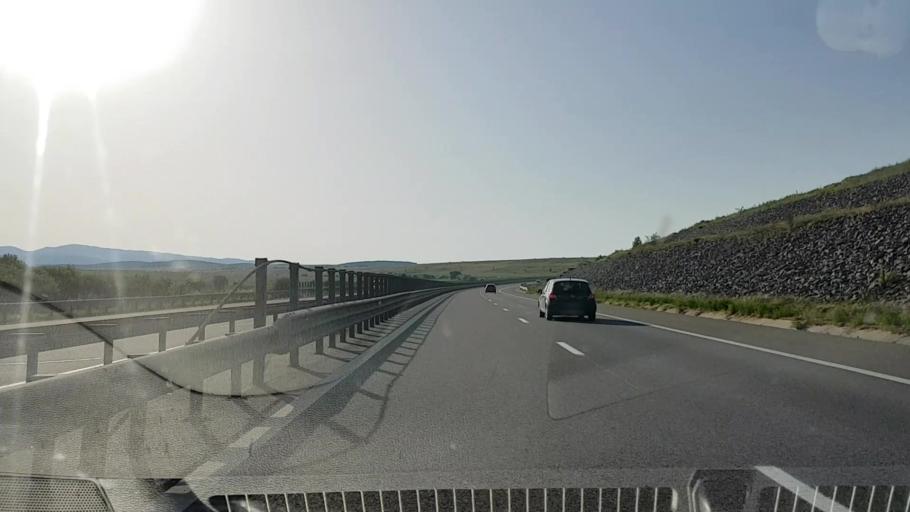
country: RO
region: Cluj
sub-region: Comuna Ciurila
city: Ciurila
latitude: 46.6427
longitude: 23.5220
